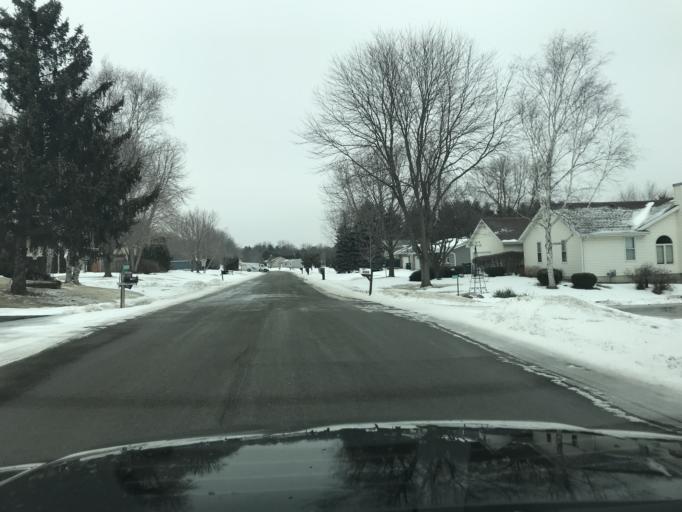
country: US
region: Wisconsin
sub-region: Dane County
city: Cottage Grove
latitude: 43.0938
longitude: -89.2161
